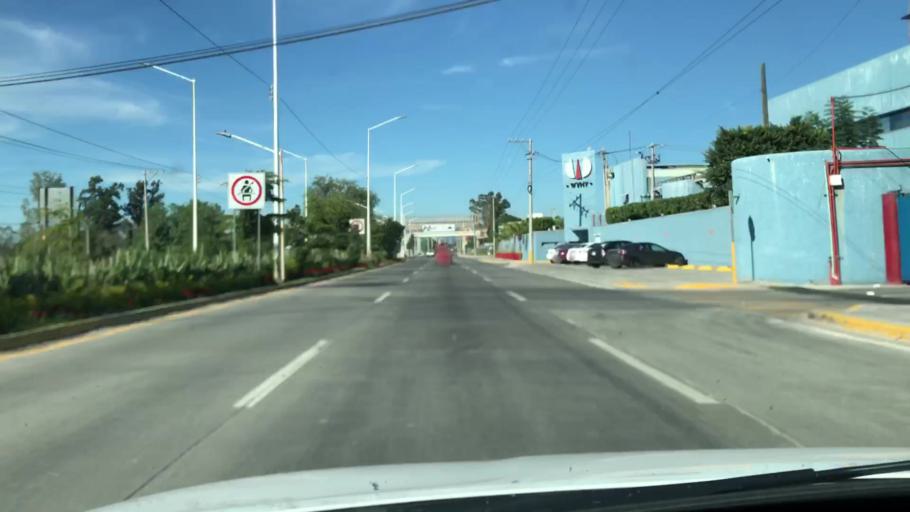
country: MX
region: Guanajuato
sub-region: Leon
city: Malagana (San Antonio del Monte)
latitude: 21.0474
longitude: -101.7884
